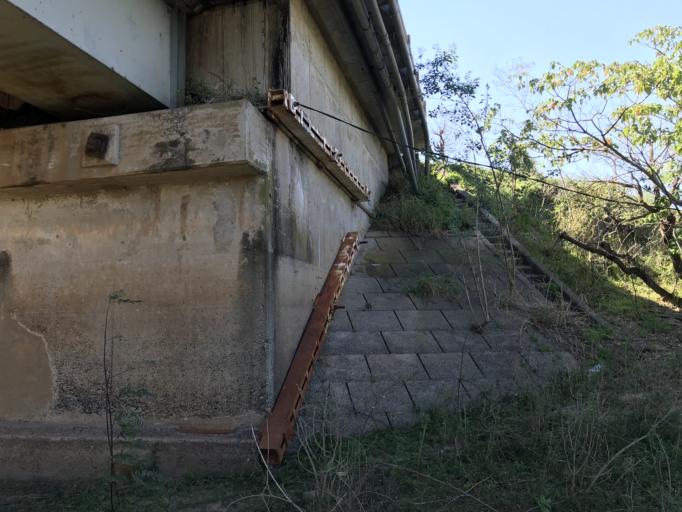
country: AR
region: Entre Rios
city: Parana
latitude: -31.6842
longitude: -60.5488
